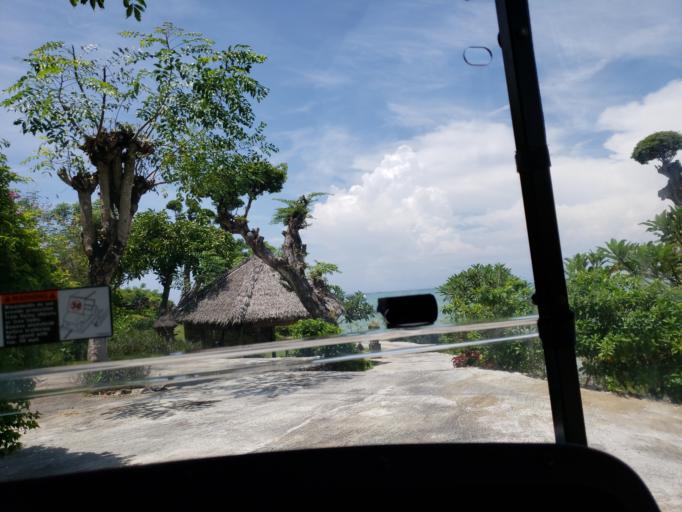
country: ID
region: Bali
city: Jimbaran
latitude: -8.7819
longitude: 115.1583
